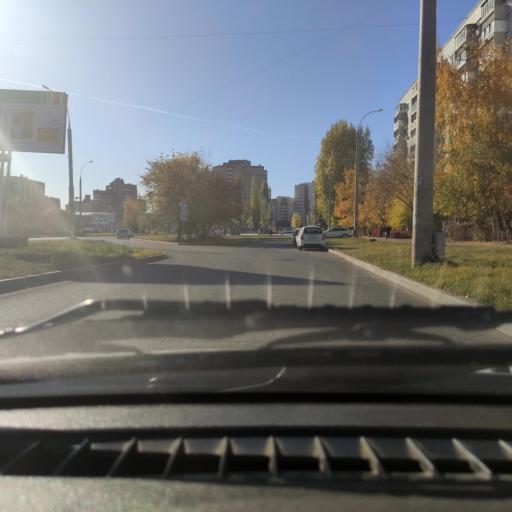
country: RU
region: Samara
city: Tol'yatti
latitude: 53.5420
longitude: 49.3602
